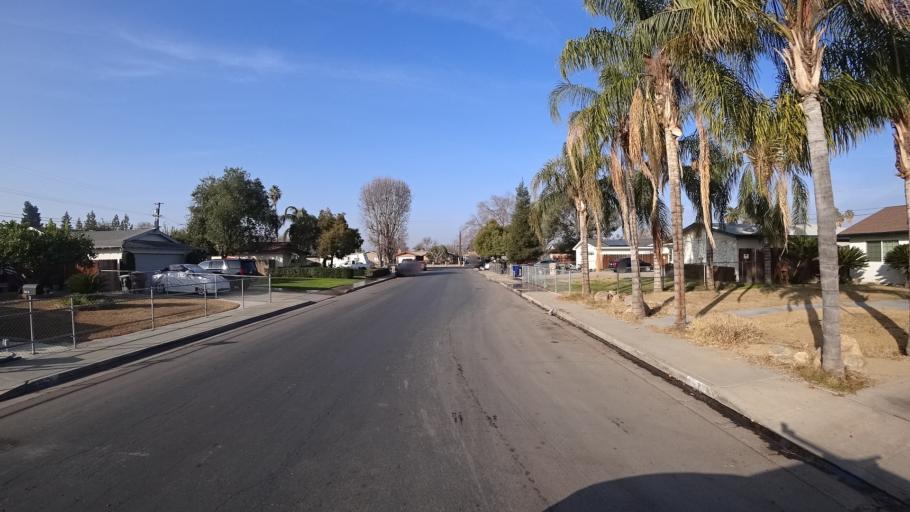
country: US
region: California
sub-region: Kern County
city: Bakersfield
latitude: 35.3347
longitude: -119.0272
